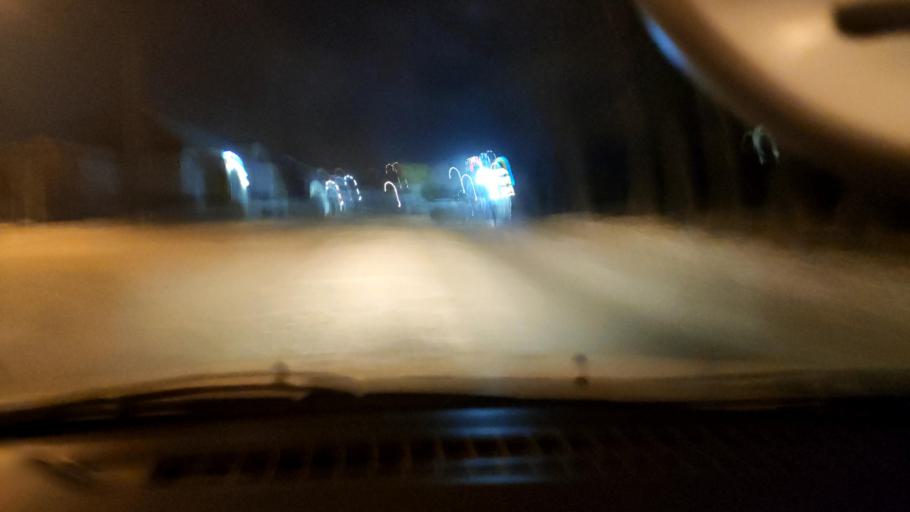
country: RU
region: Perm
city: Kultayevo
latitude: 57.9995
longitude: 55.9342
